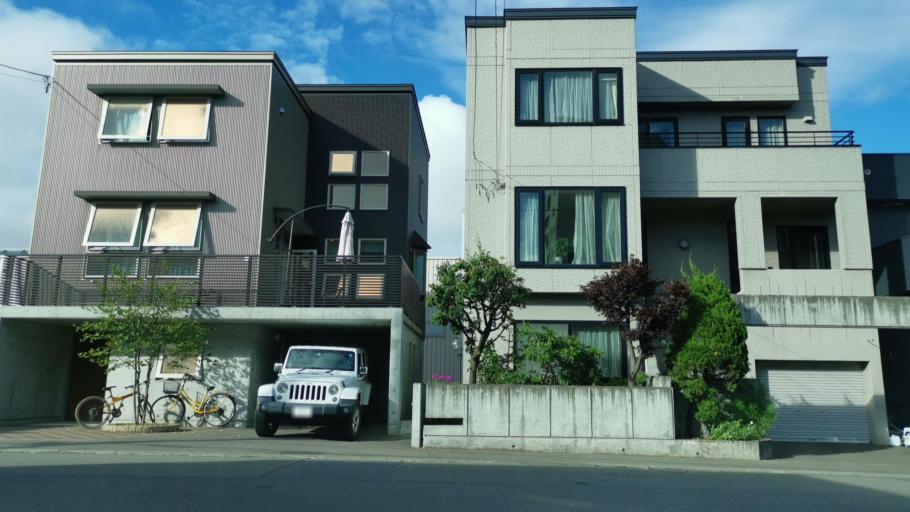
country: JP
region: Hokkaido
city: Sapporo
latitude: 43.0648
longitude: 141.2980
